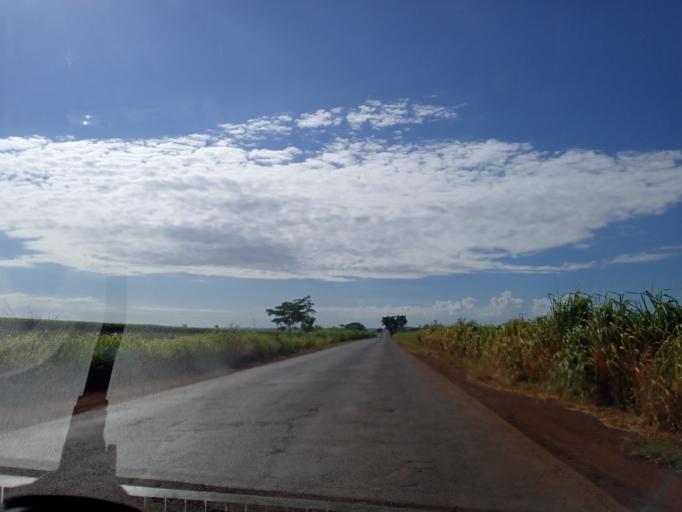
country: BR
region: Goias
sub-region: Itumbiara
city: Itumbiara
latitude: -18.4449
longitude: -49.1738
